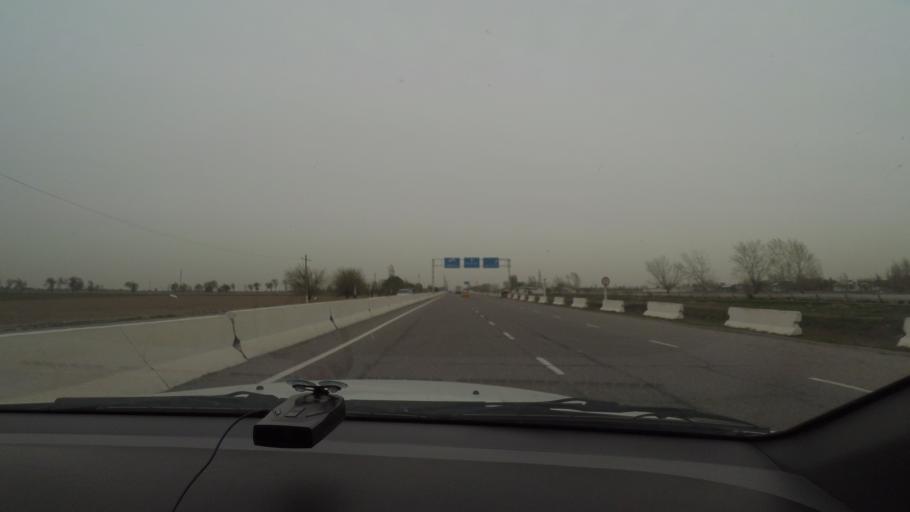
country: UZ
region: Jizzax
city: Gagarin
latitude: 40.4929
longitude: 68.2997
